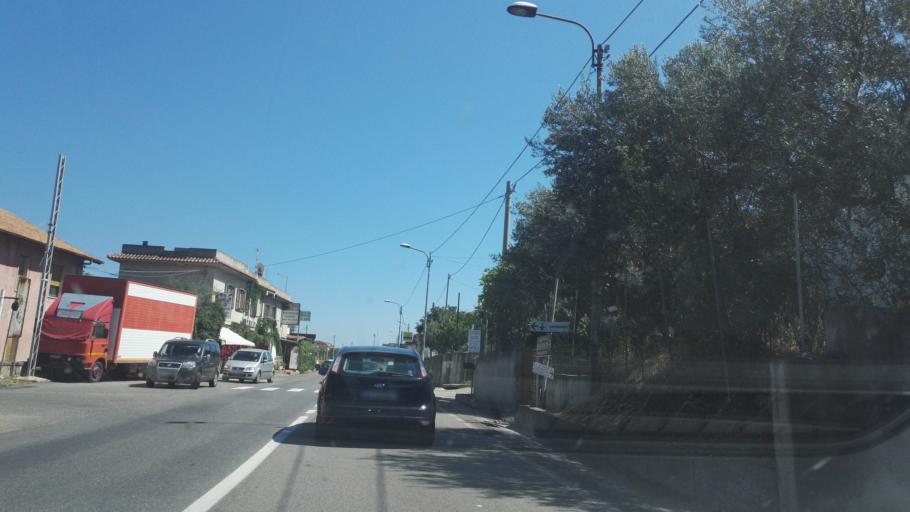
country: IT
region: Calabria
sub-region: Provincia di Cosenza
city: Borgata Marina
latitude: 39.9740
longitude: 16.6187
